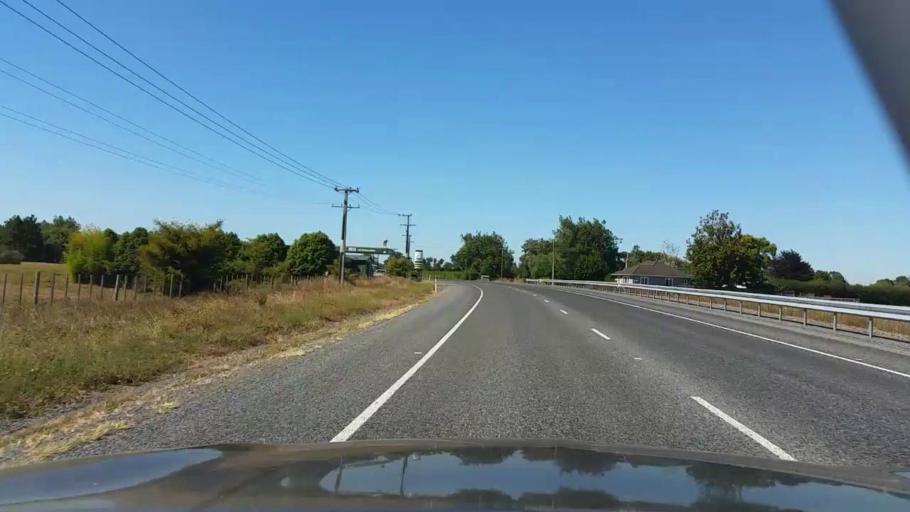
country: NZ
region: Waikato
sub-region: Hamilton City
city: Hamilton
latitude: -37.6645
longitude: 175.2989
